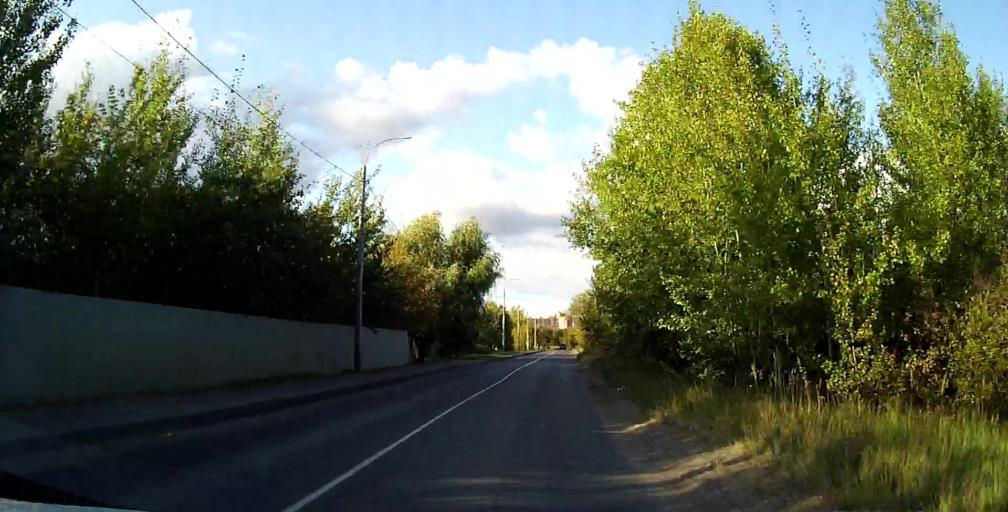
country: RU
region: Moskovskaya
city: Klimovsk
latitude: 55.3771
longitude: 37.5625
